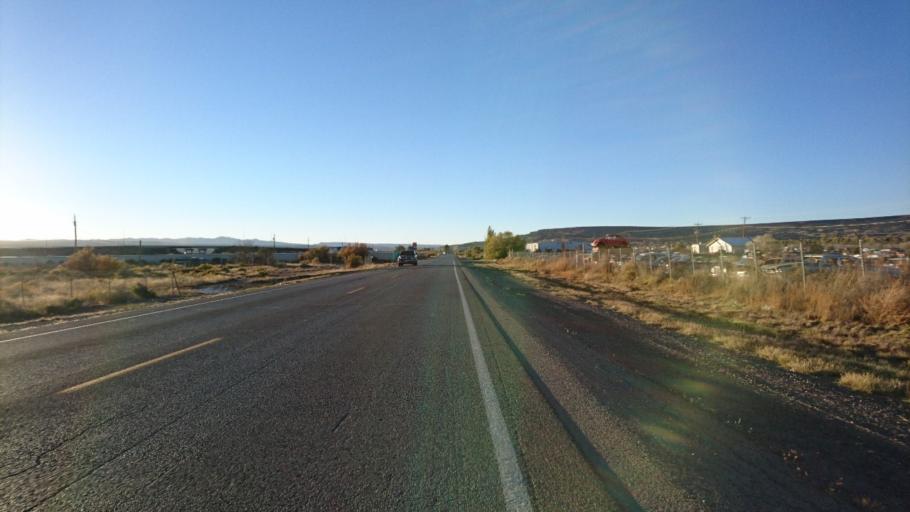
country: US
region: New Mexico
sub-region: Cibola County
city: Grants
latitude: 35.1367
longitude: -107.8225
